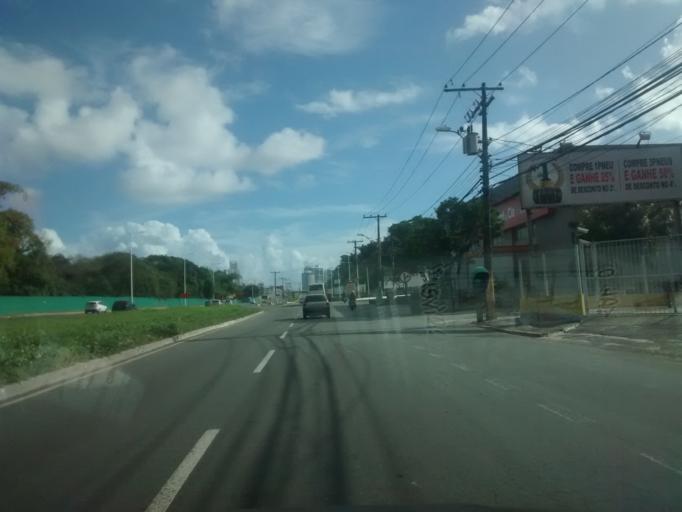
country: BR
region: Bahia
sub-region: Salvador
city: Salvador
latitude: -12.9687
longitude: -38.4418
